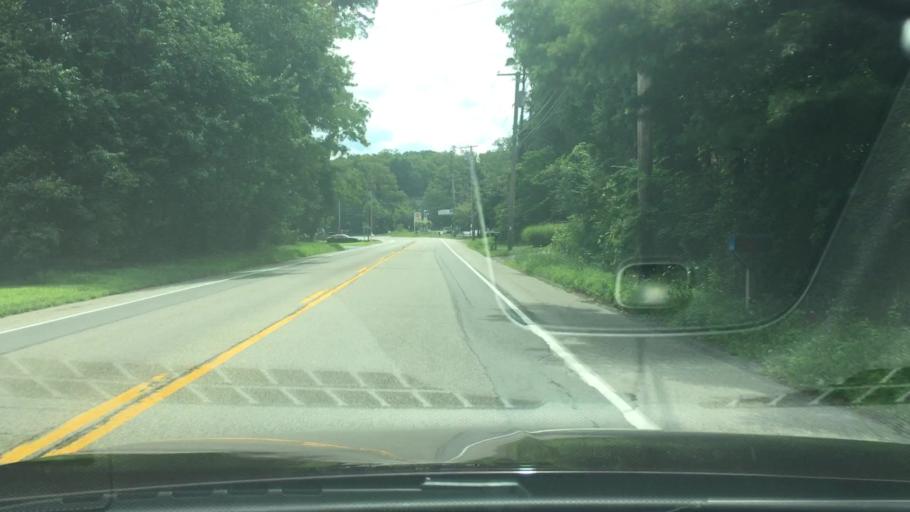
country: US
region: New York
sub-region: Dutchess County
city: Hillside Lake
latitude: 41.5536
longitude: -73.8005
